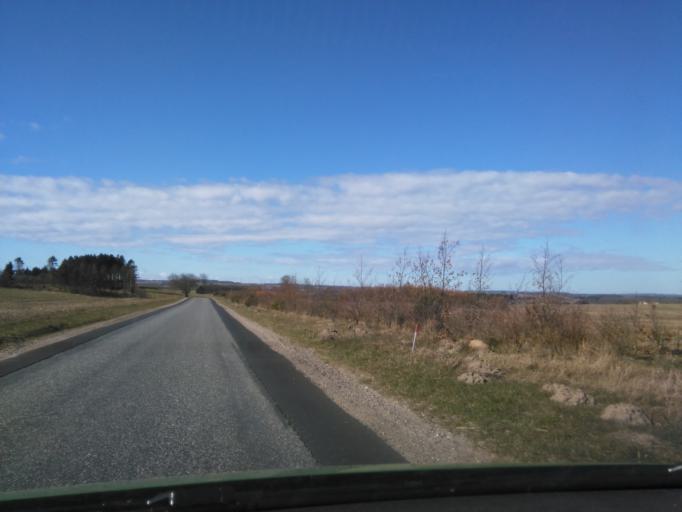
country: DK
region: Central Jutland
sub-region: Skanderborg Kommune
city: Stilling
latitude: 55.9723
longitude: 10.0212
